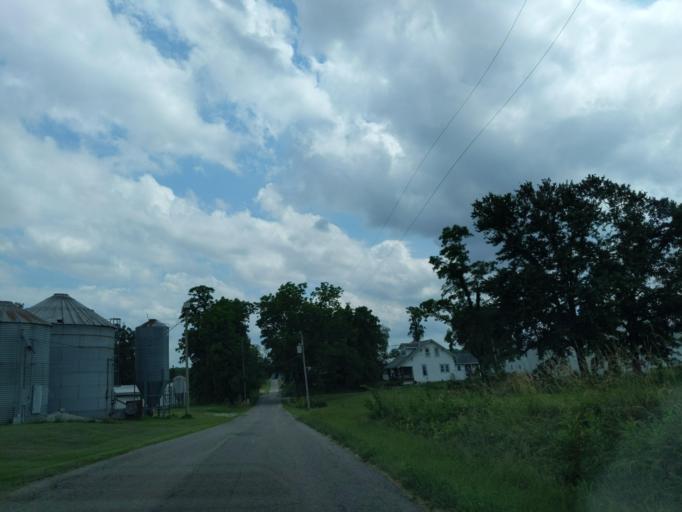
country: US
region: Indiana
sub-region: Ripley County
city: Batesville
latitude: 39.3217
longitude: -85.1898
